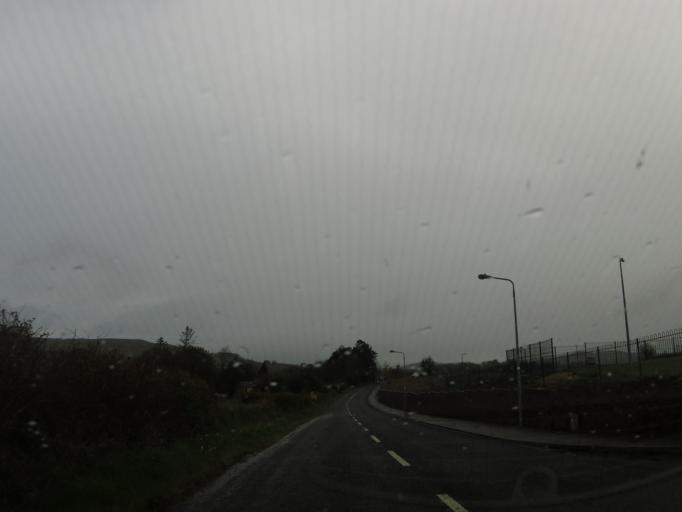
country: IE
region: Connaught
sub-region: Sligo
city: Collooney
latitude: 54.1772
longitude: -8.5056
